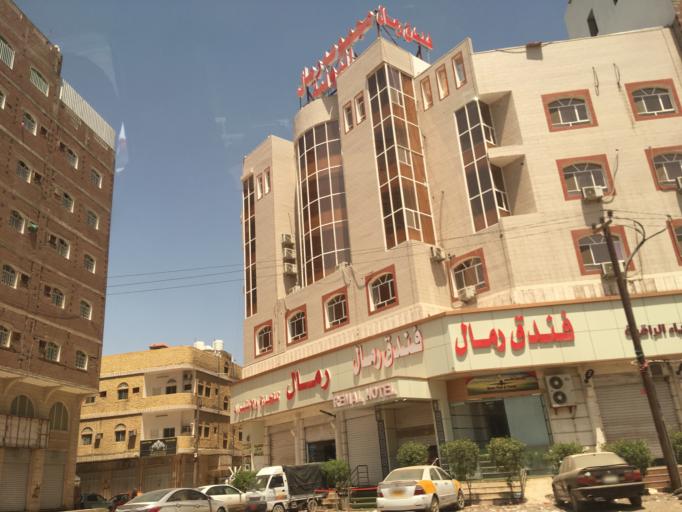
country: YE
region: Aden
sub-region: Al Mansura
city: Al Mansurah
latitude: 12.8668
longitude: 44.9709
